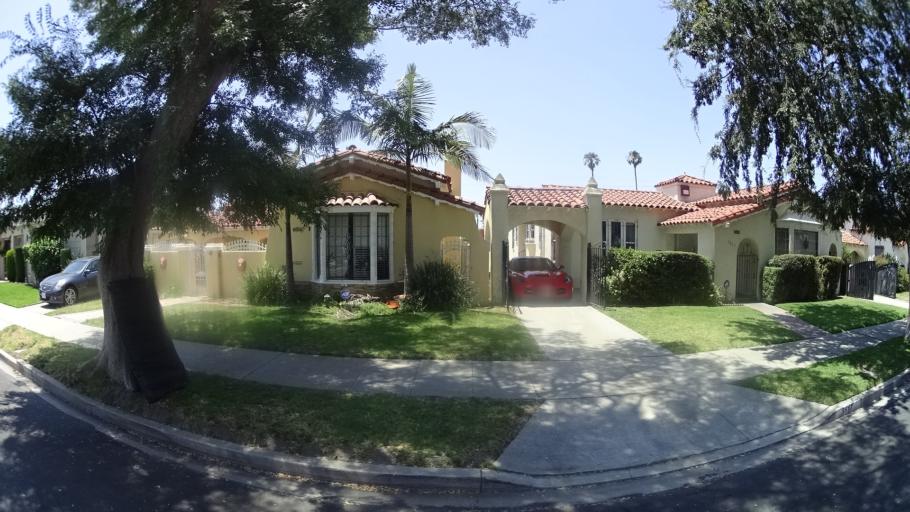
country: US
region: California
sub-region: Los Angeles County
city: View Park-Windsor Hills
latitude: 34.0168
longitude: -118.3214
